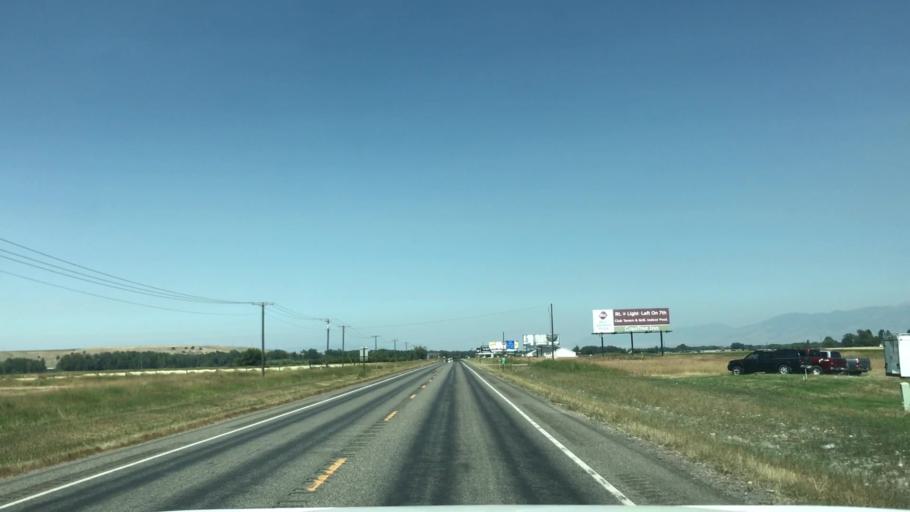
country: US
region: Montana
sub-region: Gallatin County
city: Four Corners
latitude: 45.6297
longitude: -111.1968
